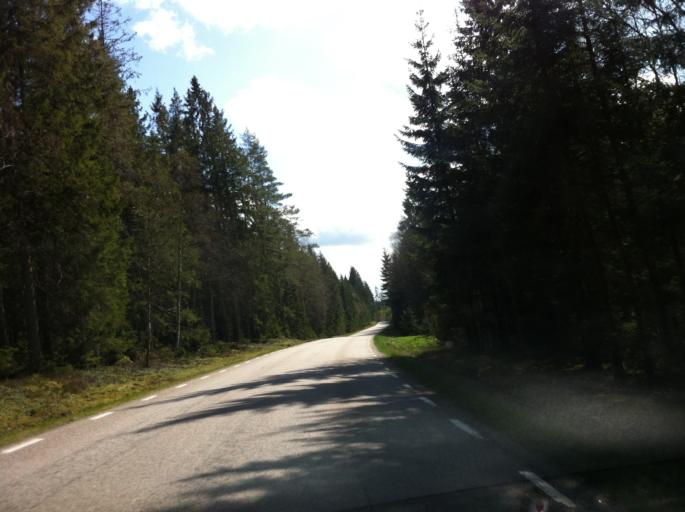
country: SE
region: Vaestra Goetaland
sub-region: Alingsas Kommun
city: Alingsas
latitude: 57.8191
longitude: 12.6441
